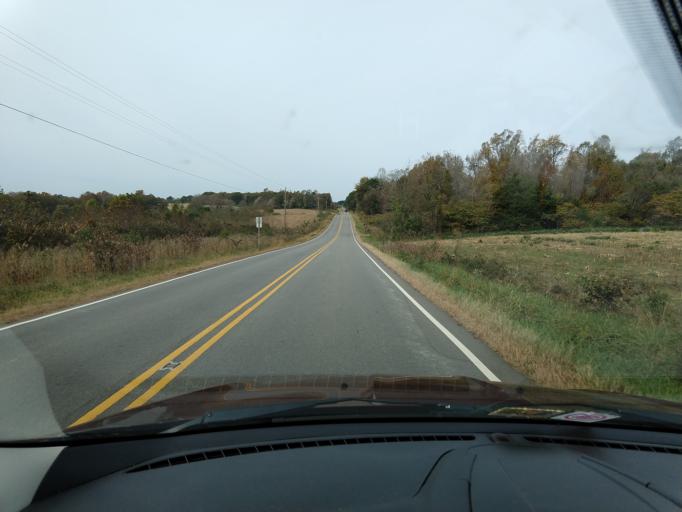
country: US
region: Virginia
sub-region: Franklin County
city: Union Hall
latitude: 36.9585
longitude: -79.5679
